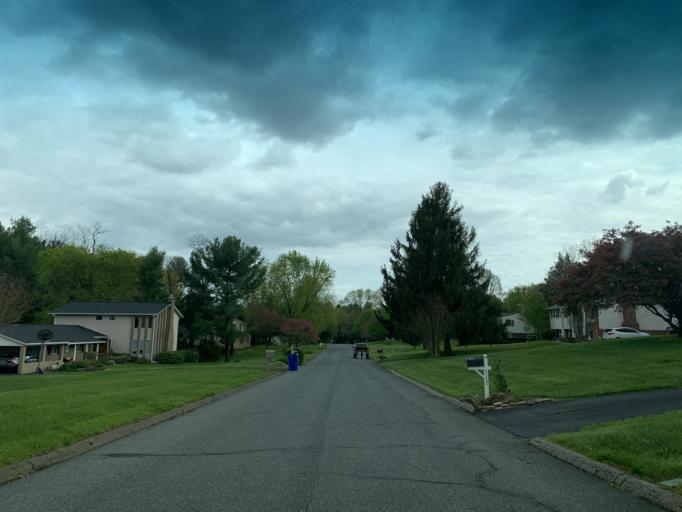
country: US
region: Maryland
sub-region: Harford County
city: Pleasant Hills
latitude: 39.4993
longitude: -76.3641
